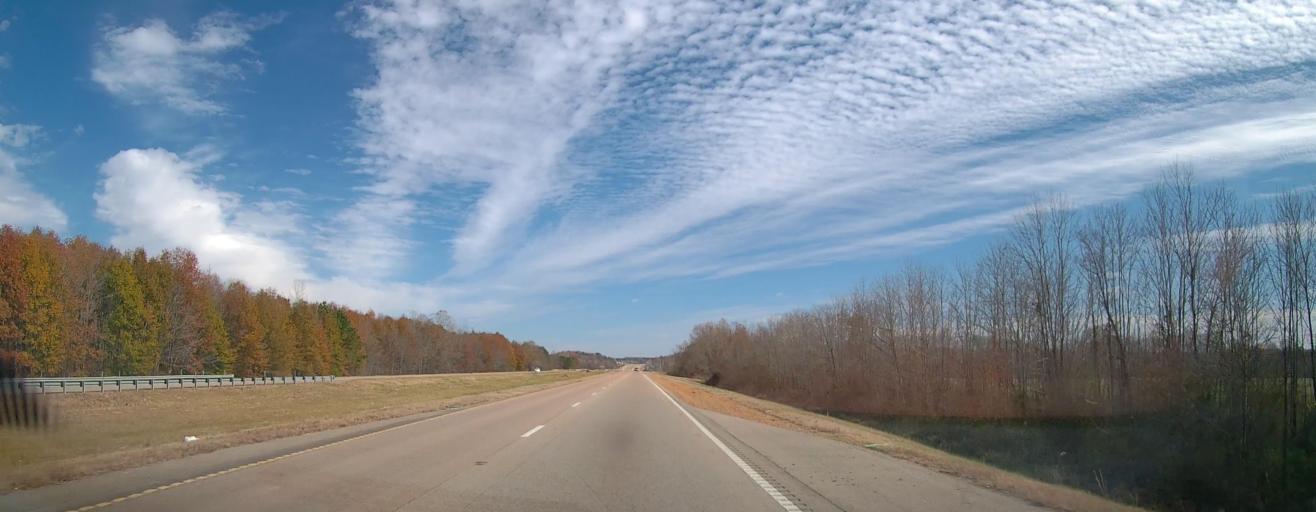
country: US
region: Mississippi
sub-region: Tippah County
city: Ripley
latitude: 34.9524
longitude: -88.8816
